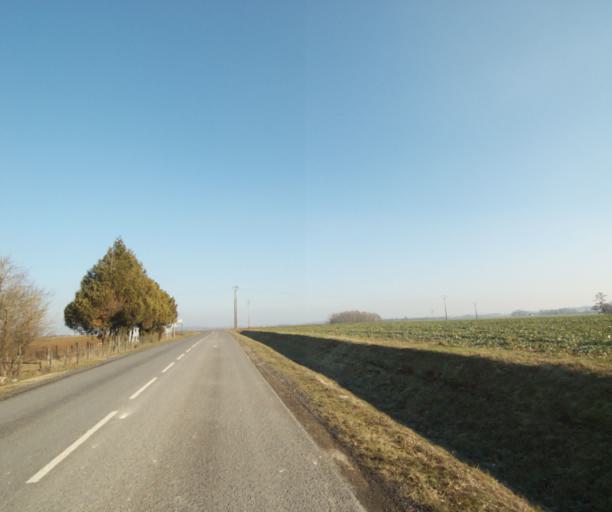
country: FR
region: Champagne-Ardenne
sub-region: Departement de la Haute-Marne
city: Wassy
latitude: 48.5001
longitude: 4.9594
